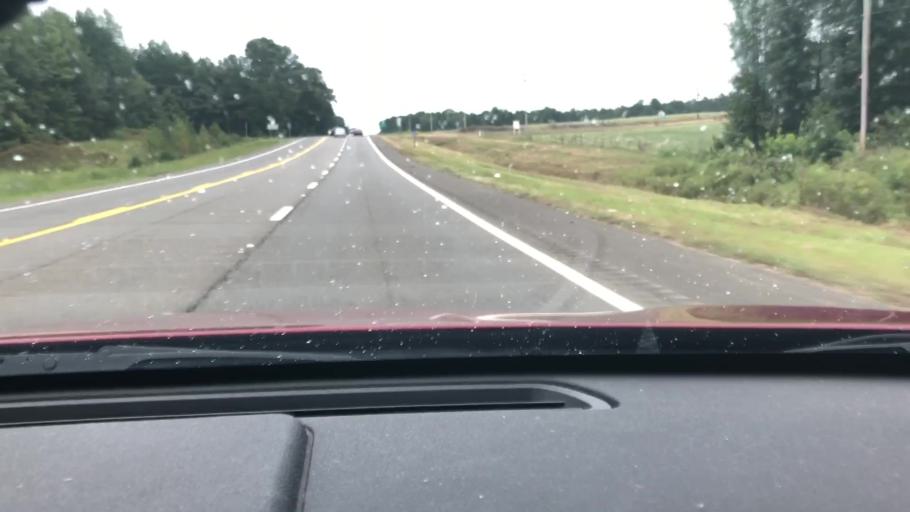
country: US
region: Arkansas
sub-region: Columbia County
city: Waldo
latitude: 33.3512
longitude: -93.3859
